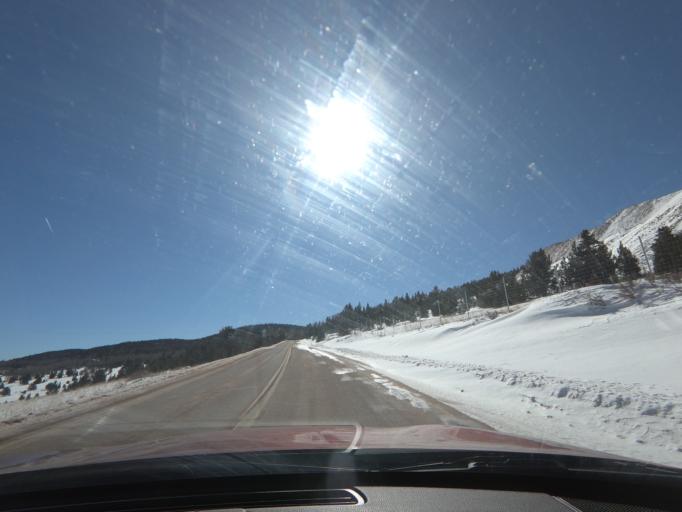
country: US
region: Colorado
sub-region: Teller County
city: Cripple Creek
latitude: 38.7409
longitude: -105.1222
